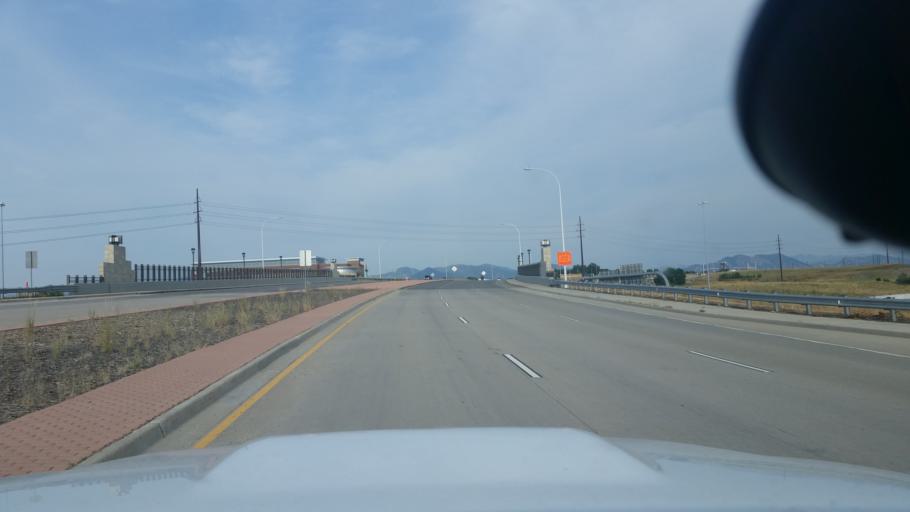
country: US
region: Colorado
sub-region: Broomfield County
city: Broomfield
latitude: 39.9116
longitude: -105.0870
